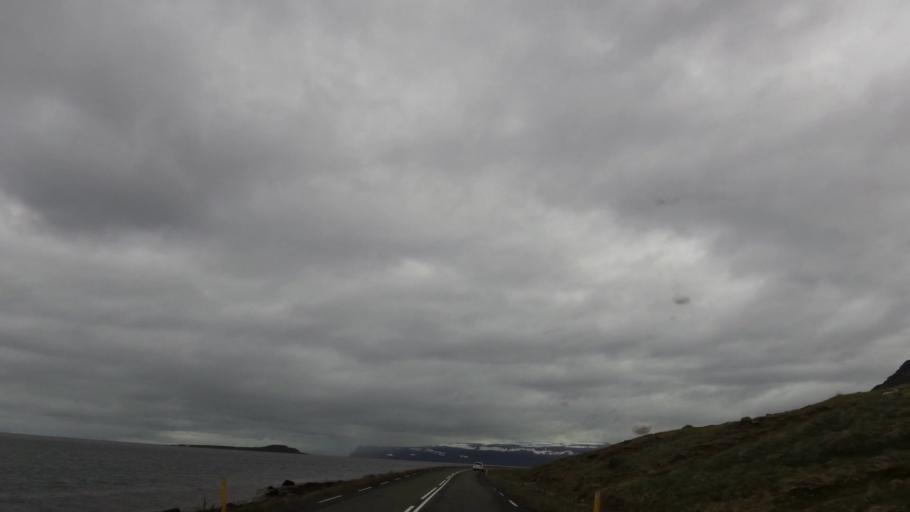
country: IS
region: Westfjords
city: Isafjoerdur
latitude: 66.0218
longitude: -22.7801
